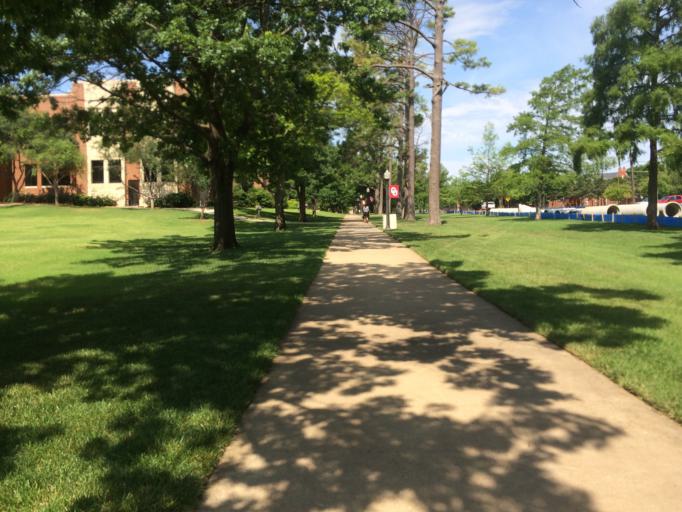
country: US
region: Oklahoma
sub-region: Cleveland County
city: Norman
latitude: 35.1964
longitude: -97.4453
